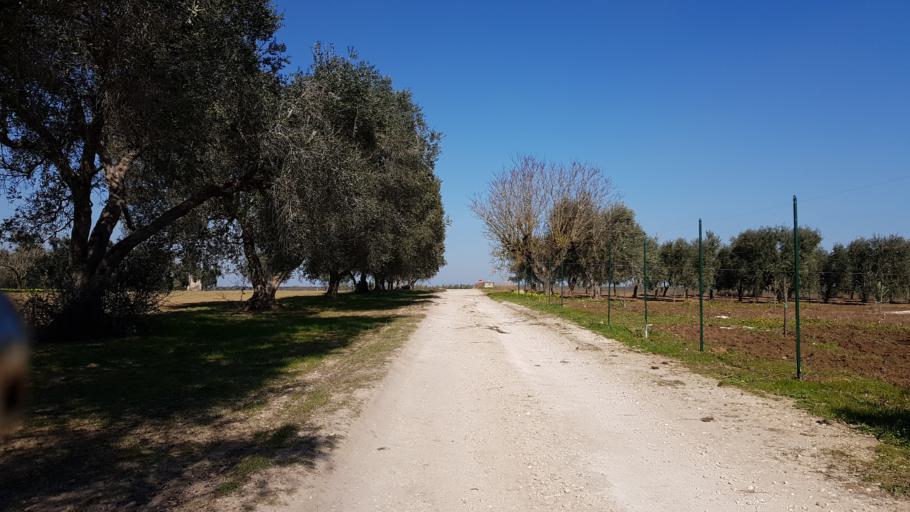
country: IT
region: Apulia
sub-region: Provincia di Brindisi
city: Mesagne
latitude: 40.6205
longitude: 17.8009
